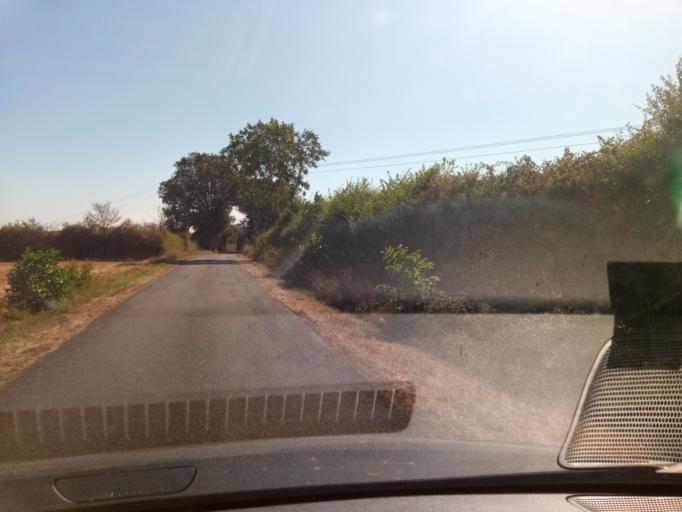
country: FR
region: Poitou-Charentes
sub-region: Departement de la Vienne
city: Lussac-les-Chateaux
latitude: 46.3987
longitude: 0.7452
